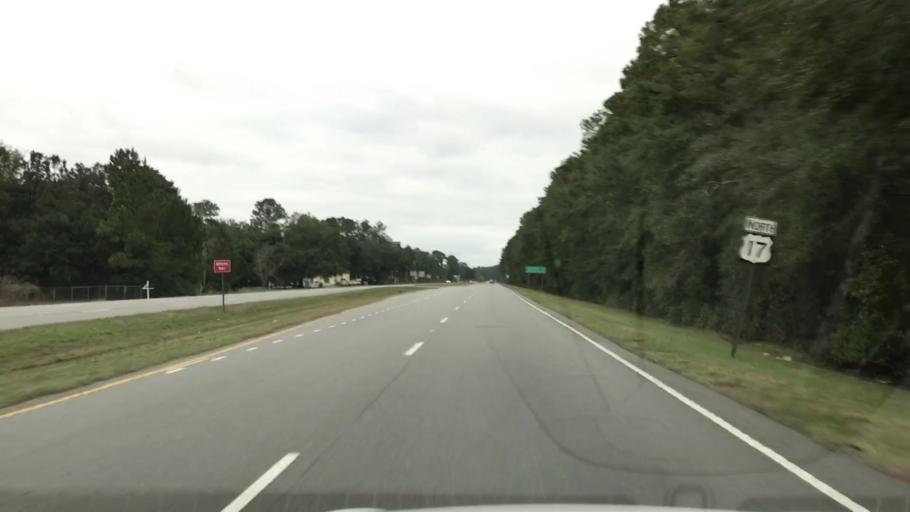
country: US
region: South Carolina
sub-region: Georgetown County
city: Georgetown
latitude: 33.2198
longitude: -79.3792
